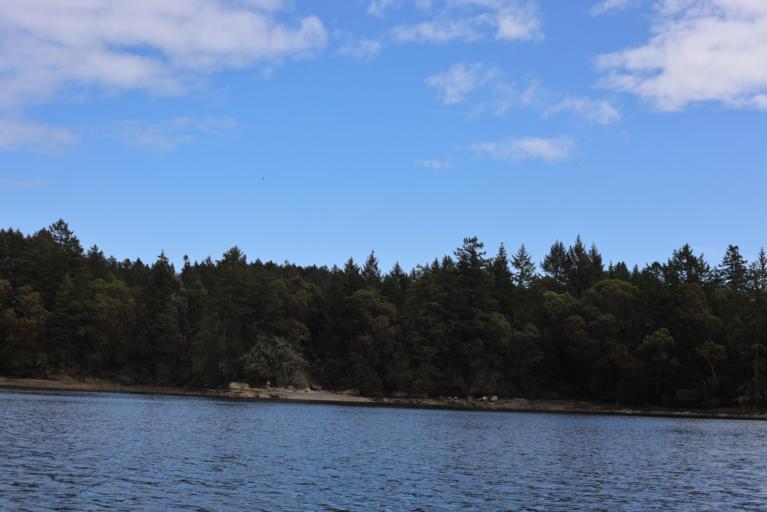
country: CA
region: British Columbia
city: North Saanich
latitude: 48.5894
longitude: -123.4688
